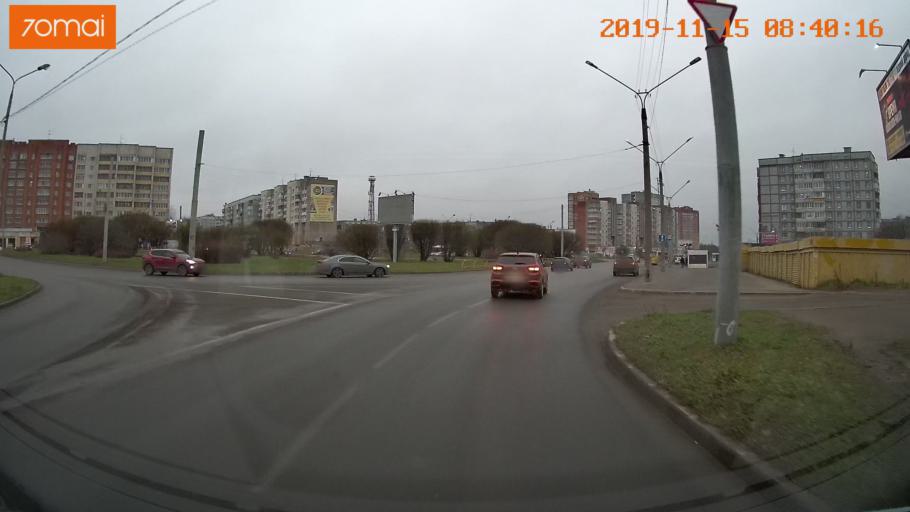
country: RU
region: Vologda
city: Cherepovets
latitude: 59.0941
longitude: 37.9158
